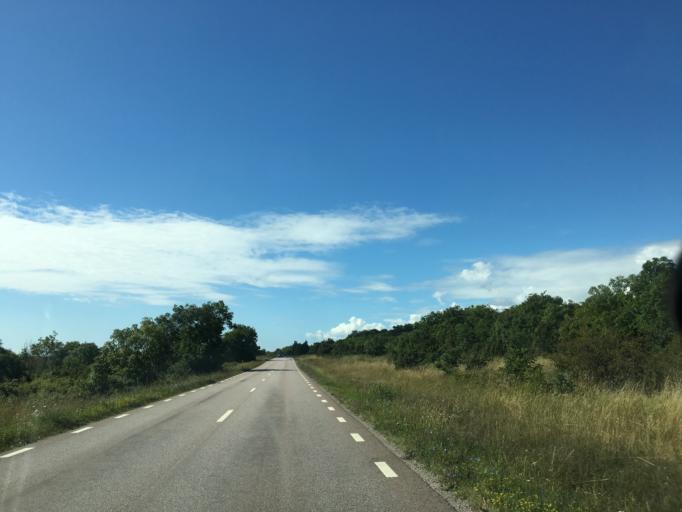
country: SE
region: Kalmar
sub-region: Morbylanga Kommun
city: Moerbylanga
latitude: 56.5645
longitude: 16.4521
